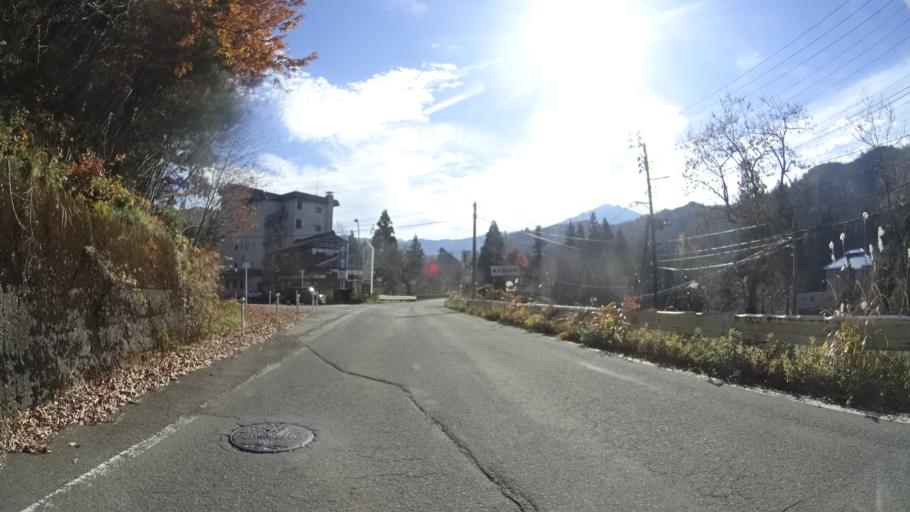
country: JP
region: Niigata
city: Muikamachi
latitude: 37.2001
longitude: 139.0762
